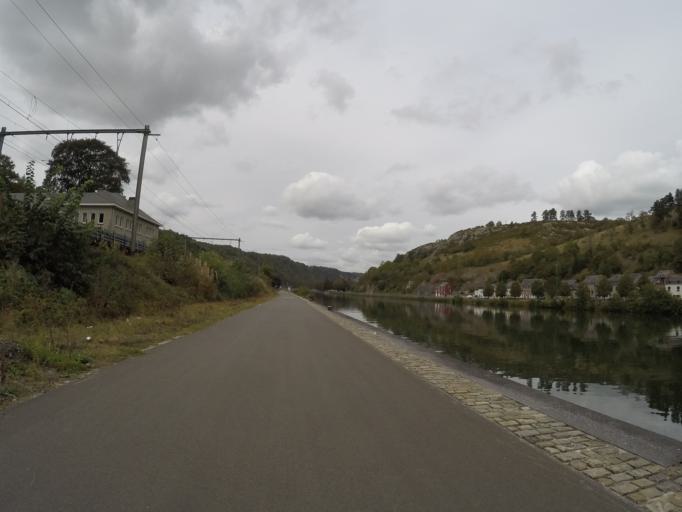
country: BE
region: Wallonia
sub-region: Province de Namur
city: Dinant
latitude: 50.2714
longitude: 4.9012
